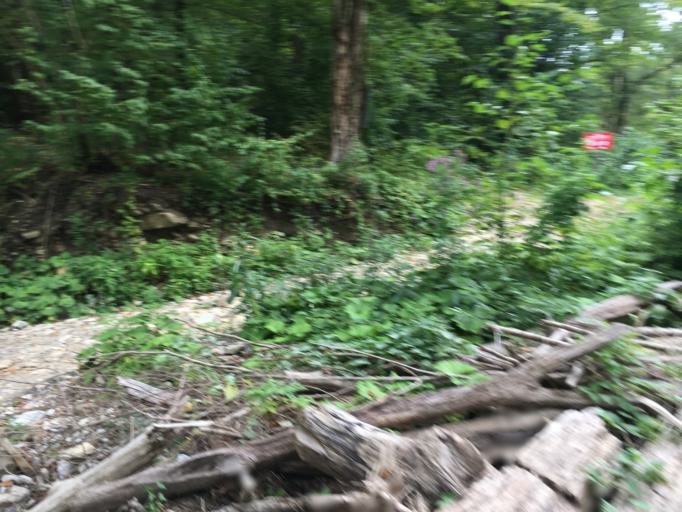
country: RU
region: Krasnodarskiy
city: Tuapse
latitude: 44.2571
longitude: 39.2198
